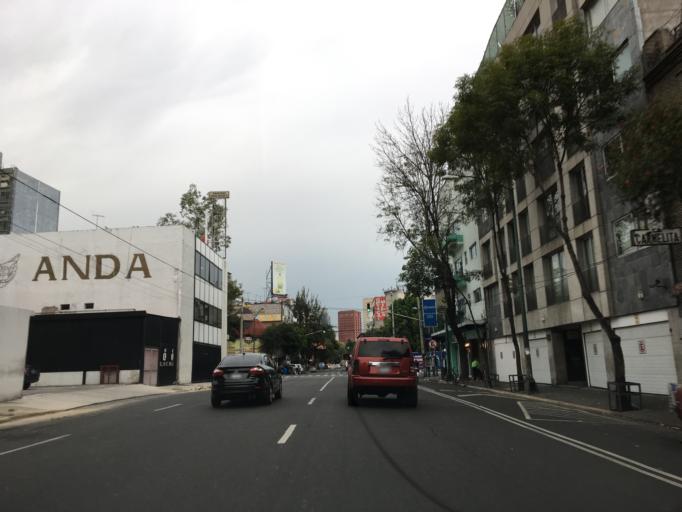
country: MX
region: Mexico City
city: Cuauhtemoc
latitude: 19.4351
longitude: -99.1628
